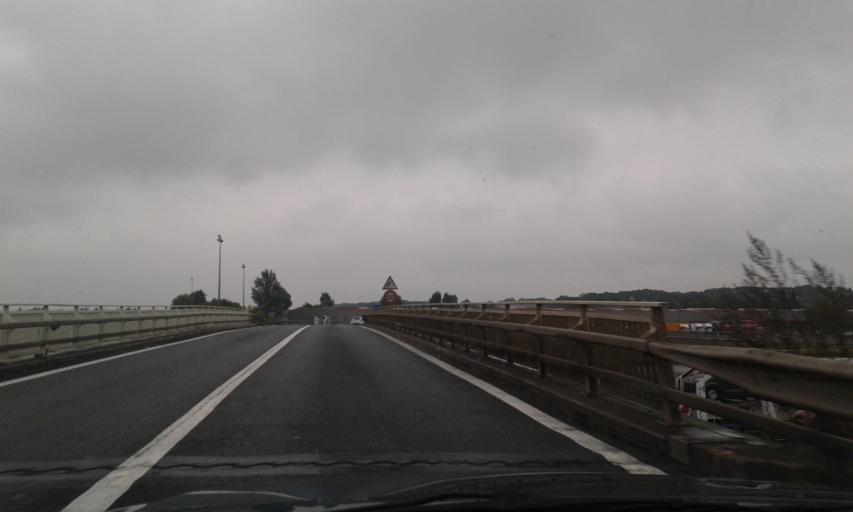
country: FR
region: Centre
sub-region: Departement du Loiret
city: Saran
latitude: 47.9501
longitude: 1.8497
